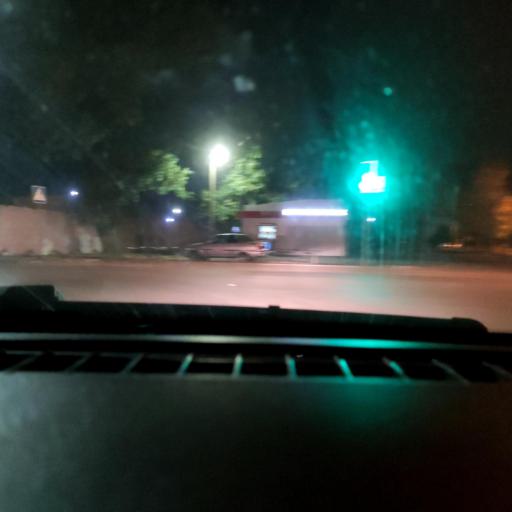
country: RU
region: Voronezj
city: Maslovka
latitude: 51.6339
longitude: 39.2635
